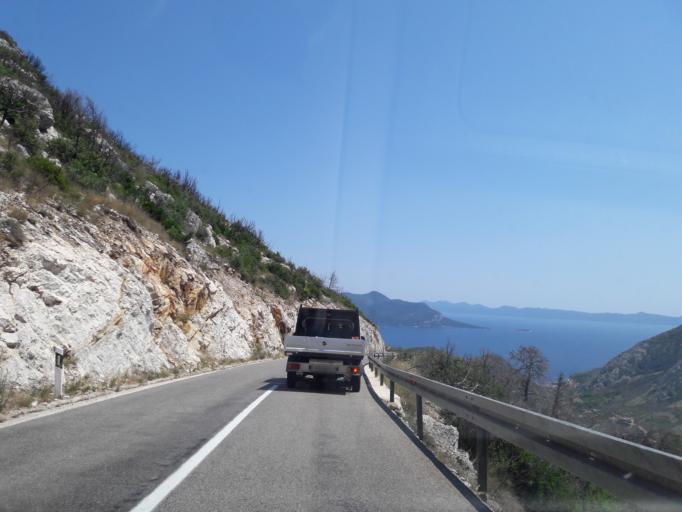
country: HR
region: Dubrovacko-Neretvanska
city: Komin
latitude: 42.9363
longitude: 17.3881
